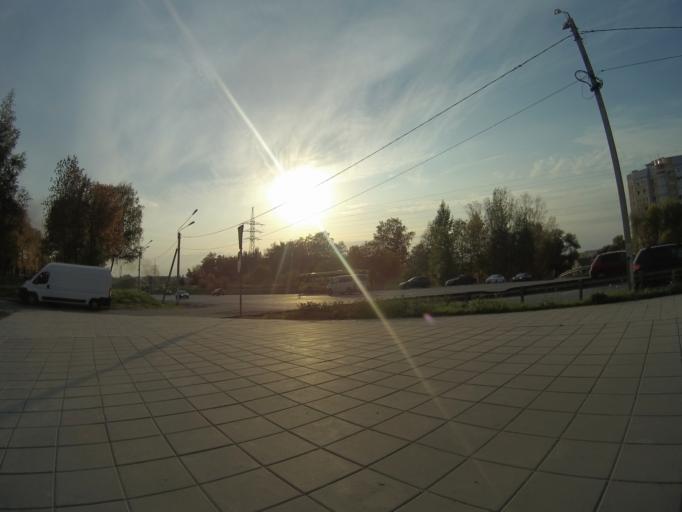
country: RU
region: Vladimir
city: Vladimir
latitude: 56.1584
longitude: 40.3754
